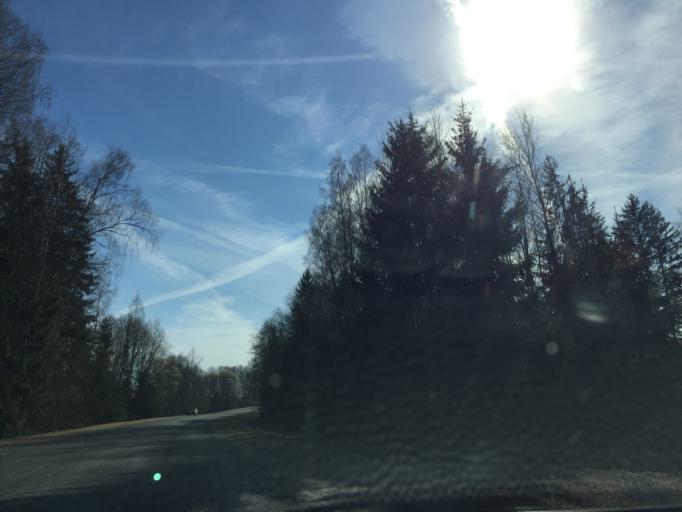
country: EE
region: Vorumaa
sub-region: Antsla vald
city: Vana-Antsla
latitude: 57.9976
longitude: 26.4232
